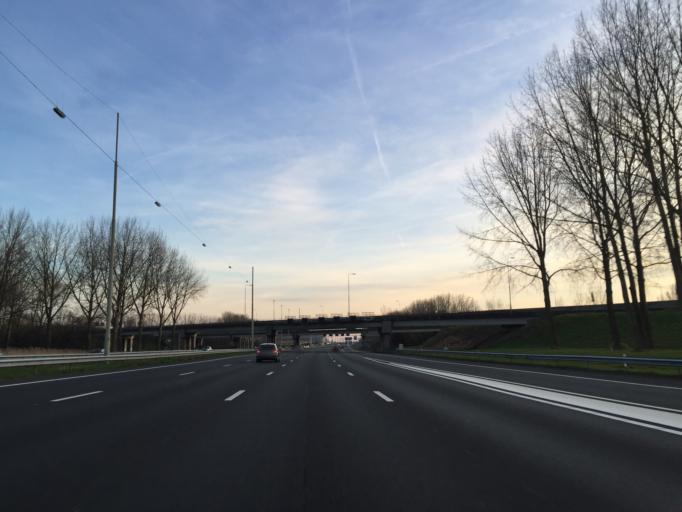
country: NL
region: South Holland
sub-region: Gemeente Ridderkerk
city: Ridderkerk
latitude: 51.8582
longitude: 4.5961
